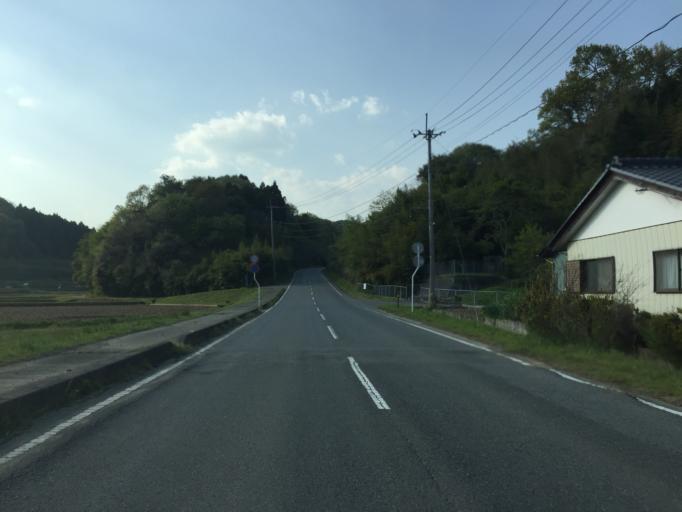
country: JP
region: Fukushima
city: Iwaki
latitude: 36.9685
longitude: 140.8396
